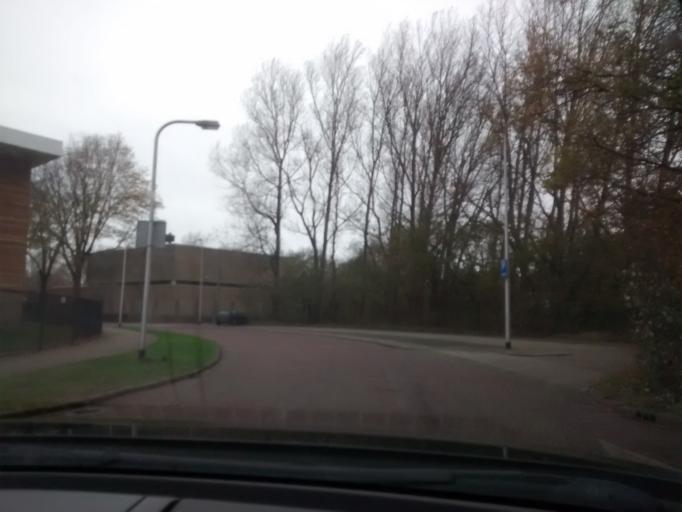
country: NL
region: South Holland
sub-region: Gemeente Katwijk
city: Katwijk aan den Rijn
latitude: 52.1970
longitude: 4.4186
